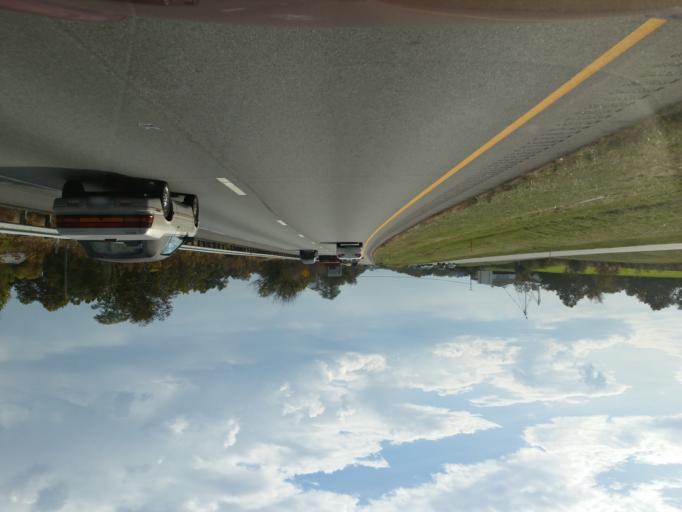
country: US
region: Pennsylvania
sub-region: Lancaster County
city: Mount Joy
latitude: 40.1308
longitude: -76.4897
